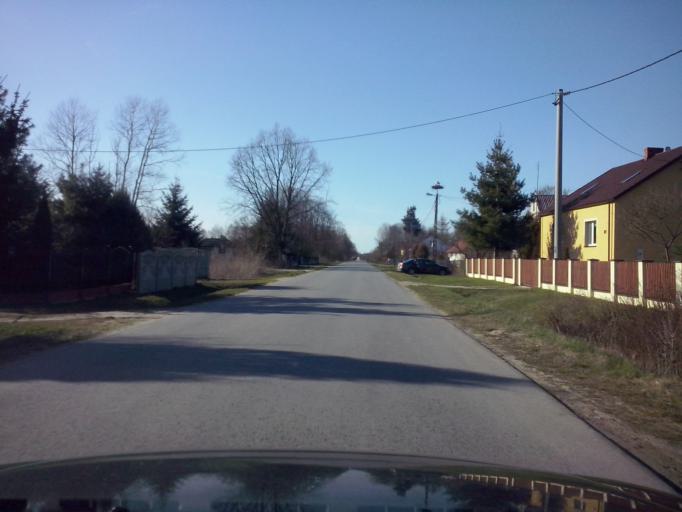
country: PL
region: Subcarpathian Voivodeship
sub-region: Powiat lezajski
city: Stare Miasto
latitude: 50.3500
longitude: 22.4256
